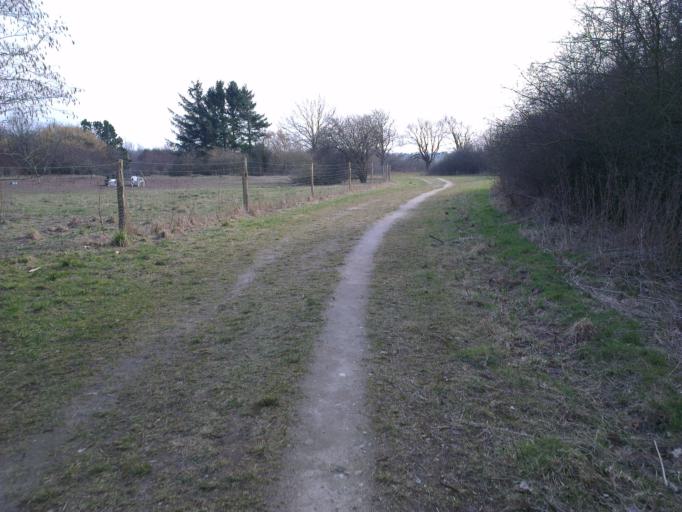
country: DK
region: Capital Region
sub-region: Frederikssund Kommune
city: Frederikssund
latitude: 55.8370
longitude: 12.0891
